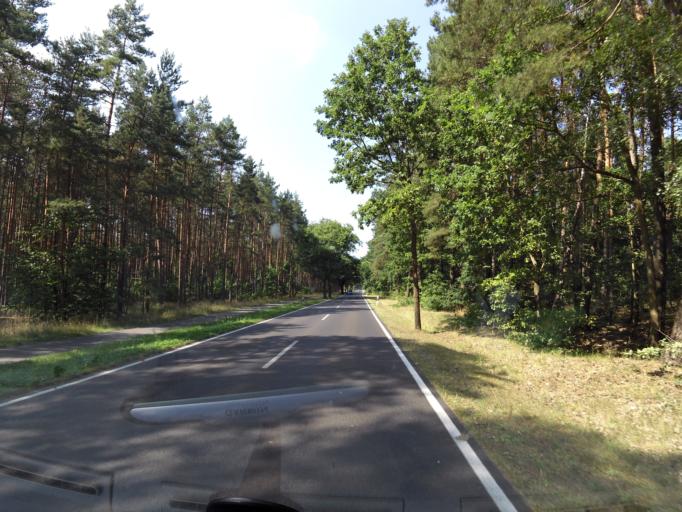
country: DE
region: Brandenburg
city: Zehdenick
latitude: 52.9696
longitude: 13.3594
